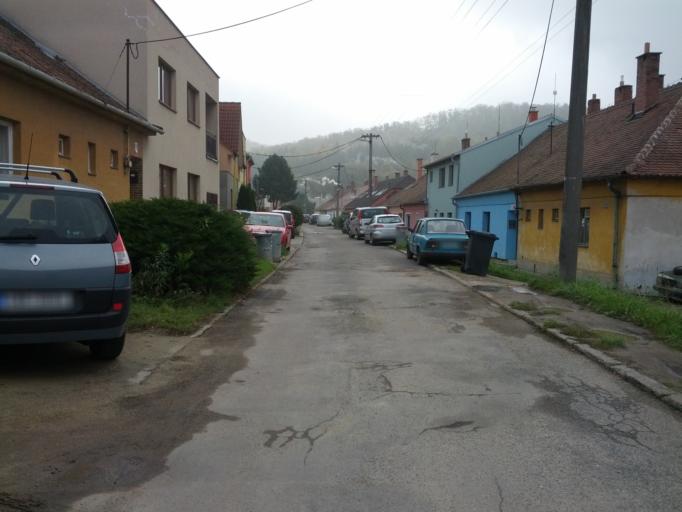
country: CZ
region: South Moravian
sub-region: Okres Brno-Venkov
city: Lelekovice
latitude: 49.3046
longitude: 16.5585
